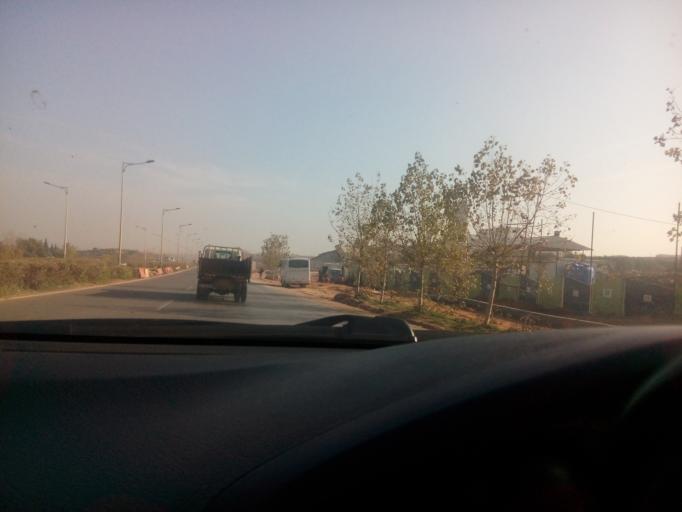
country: DZ
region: Oran
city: Oran
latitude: 35.6521
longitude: -0.6877
